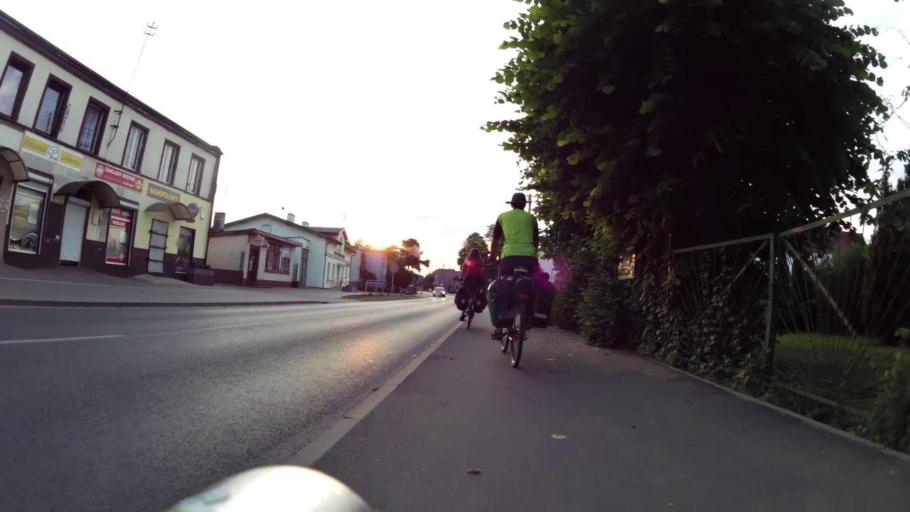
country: PL
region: Kujawsko-Pomorskie
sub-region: Powiat bydgoski
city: Dabrowa Chelminska
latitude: 53.1764
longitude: 18.3022
